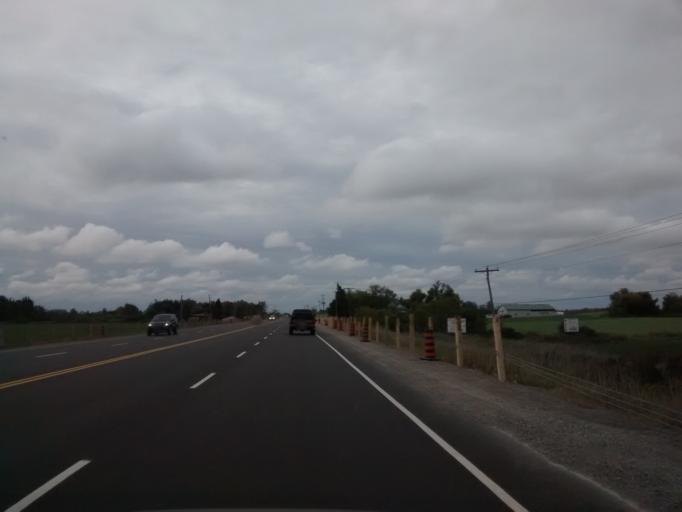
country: CA
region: Ontario
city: Ancaster
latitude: 43.1284
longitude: -79.9273
